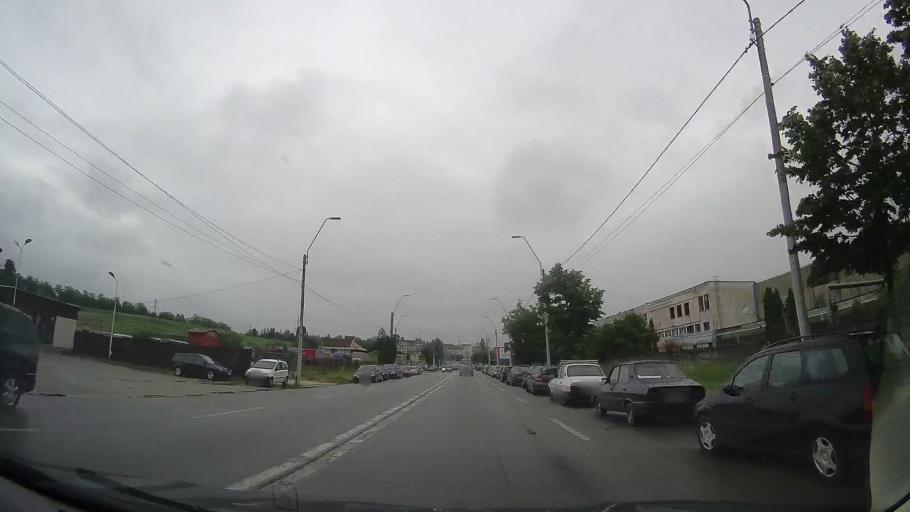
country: RO
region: Mehedinti
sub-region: Municipiul Drobeta-Turnu Severin
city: Drobeta-Turnu Severin
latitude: 44.6239
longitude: 22.6324
